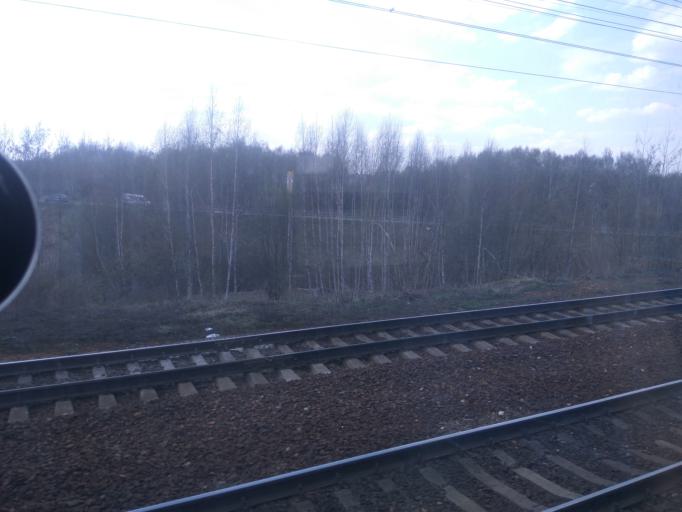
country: RU
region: Moskovskaya
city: Yakhroma
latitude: 56.2963
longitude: 37.4968
